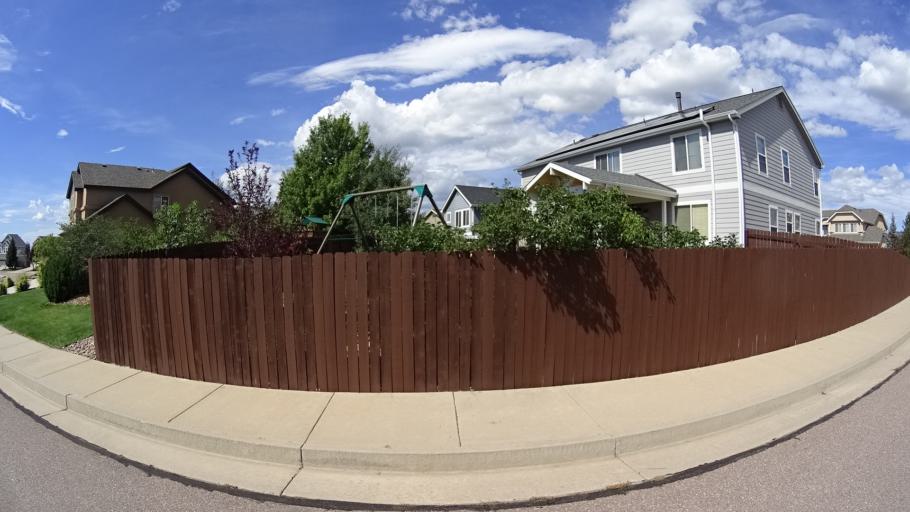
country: US
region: Colorado
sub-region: El Paso County
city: Gleneagle
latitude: 39.0299
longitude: -104.8200
